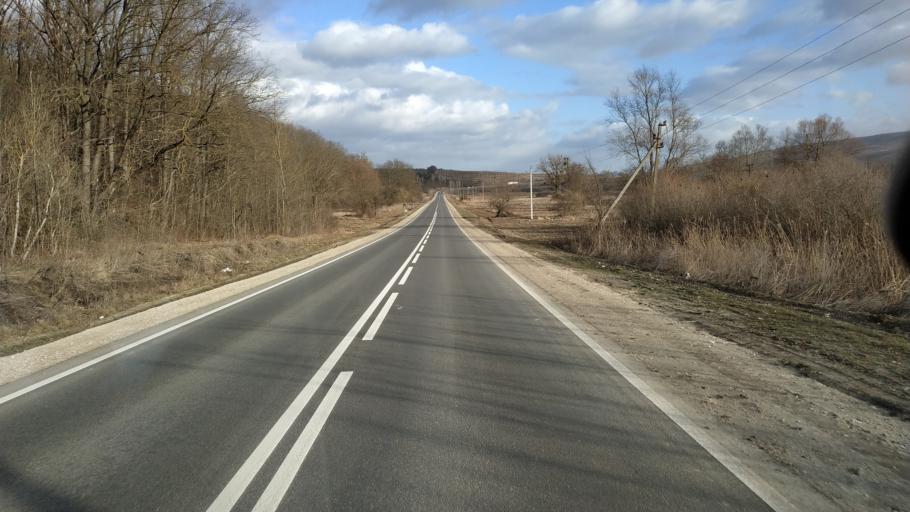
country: MD
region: Calarasi
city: Calarasi
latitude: 47.3027
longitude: 28.1406
